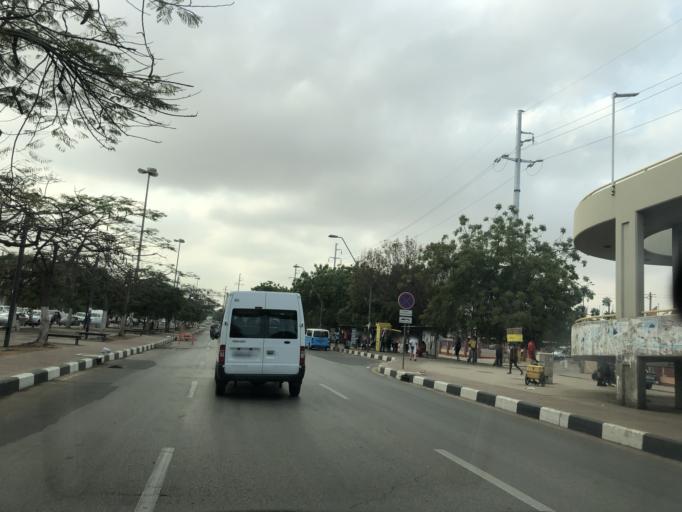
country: AO
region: Luanda
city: Luanda
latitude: -8.8320
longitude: 13.2516
